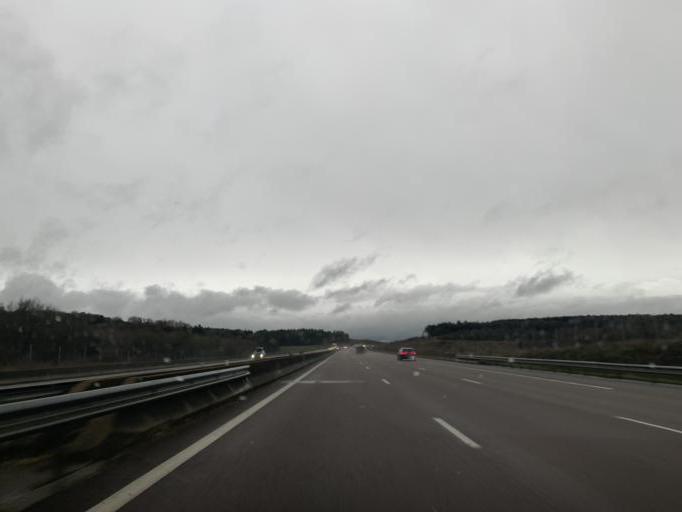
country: FR
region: Champagne-Ardenne
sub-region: Departement de la Haute-Marne
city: Rolampont
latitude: 47.8647
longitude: 5.2227
